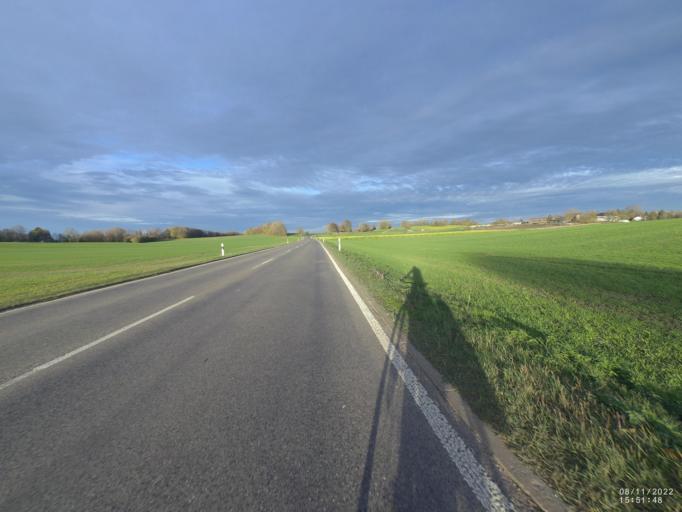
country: DE
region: Baden-Wuerttemberg
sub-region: Regierungsbezirk Stuttgart
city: Bad Uberkingen
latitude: 48.5897
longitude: 9.8084
